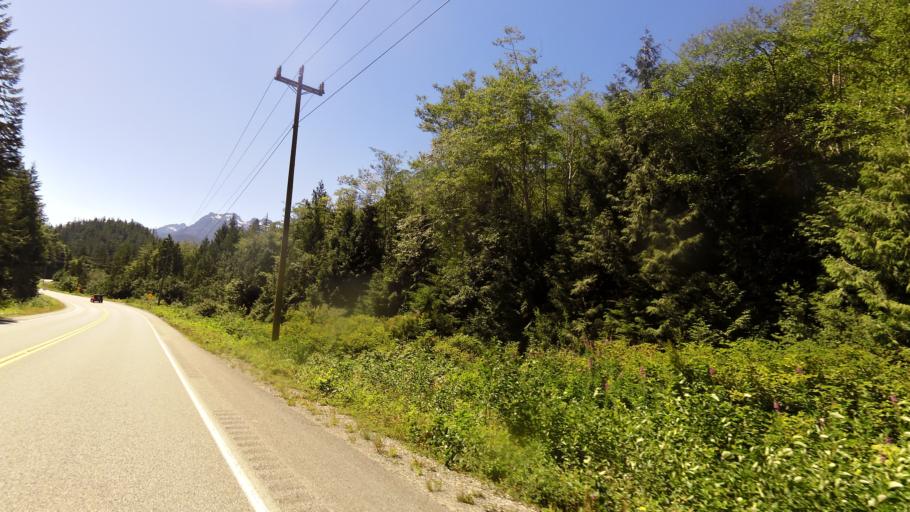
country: CA
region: British Columbia
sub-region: Regional District of Alberni-Clayoquot
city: Ucluelet
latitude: 49.2110
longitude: -125.3714
